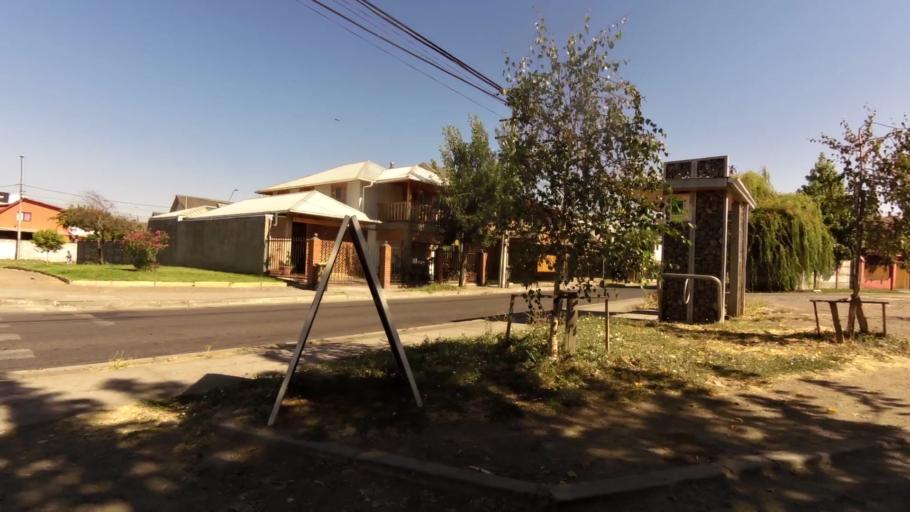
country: CL
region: Maule
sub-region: Provincia de Curico
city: Curico
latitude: -34.9776
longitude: -71.2650
